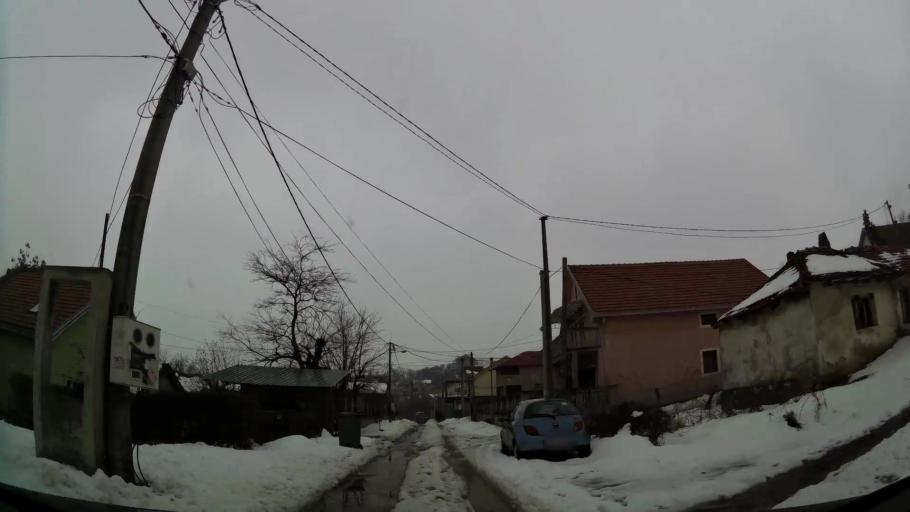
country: RS
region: Central Serbia
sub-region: Belgrade
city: Zvezdara
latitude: 44.7466
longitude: 20.5190
